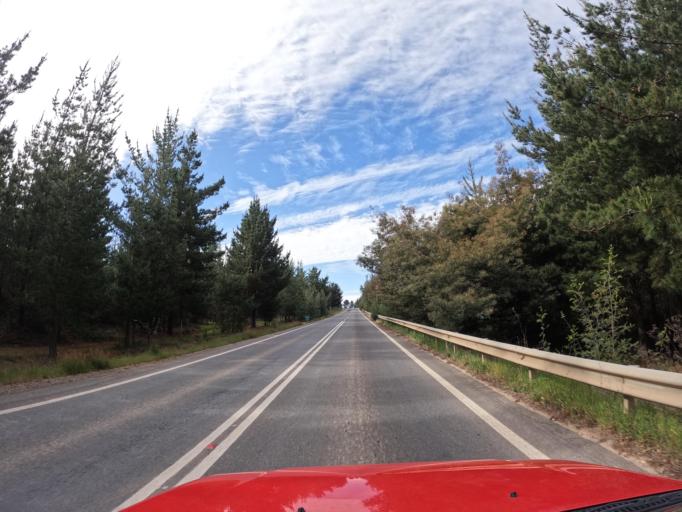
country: CL
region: O'Higgins
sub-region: Provincia de Colchagua
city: Santa Cruz
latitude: -34.3121
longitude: -71.8520
